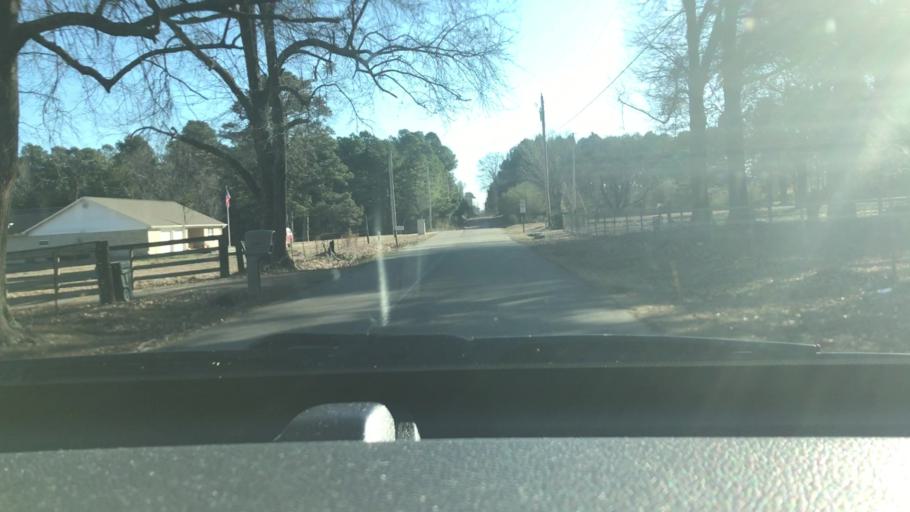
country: US
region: Arkansas
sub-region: Hempstead County
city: Hope
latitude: 33.6388
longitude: -93.5740
